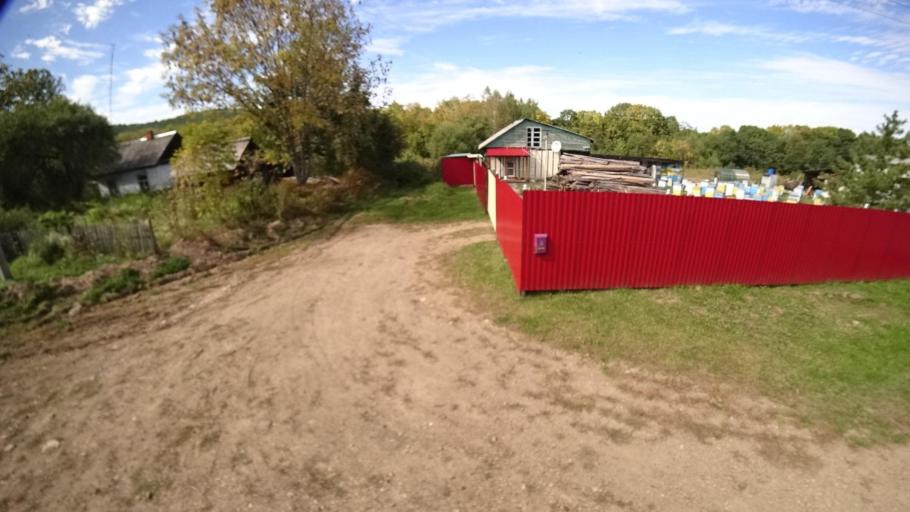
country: RU
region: Primorskiy
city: Yakovlevka
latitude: 44.3933
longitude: 133.6026
